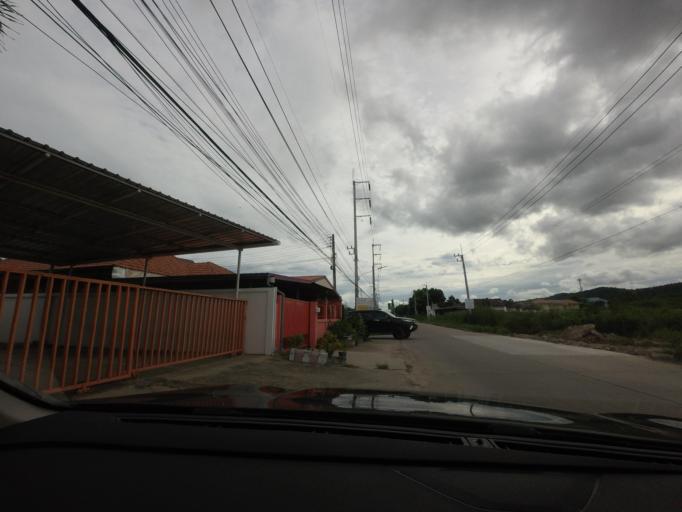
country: TH
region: Prachuap Khiri Khan
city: Hua Hin
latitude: 12.5396
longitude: 99.9485
